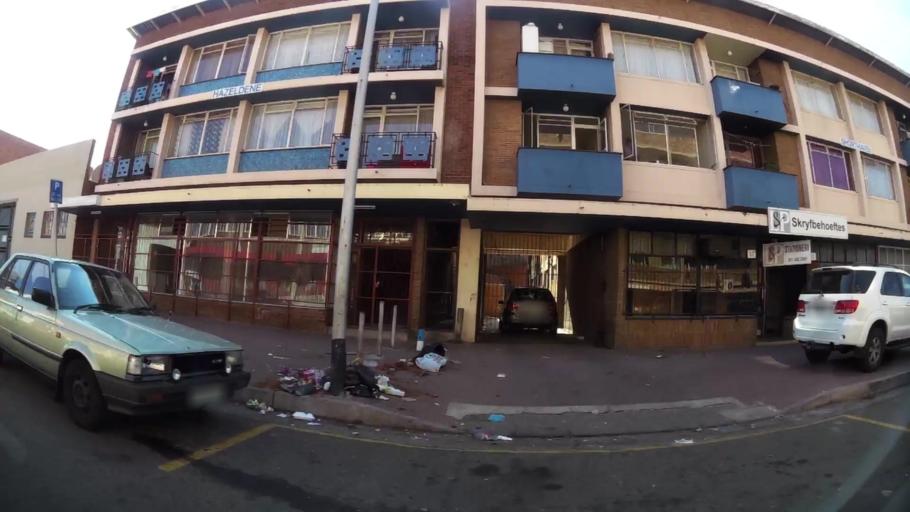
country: ZA
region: Orange Free State
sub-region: Mangaung Metropolitan Municipality
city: Bloemfontein
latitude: -29.1117
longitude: 26.2227
